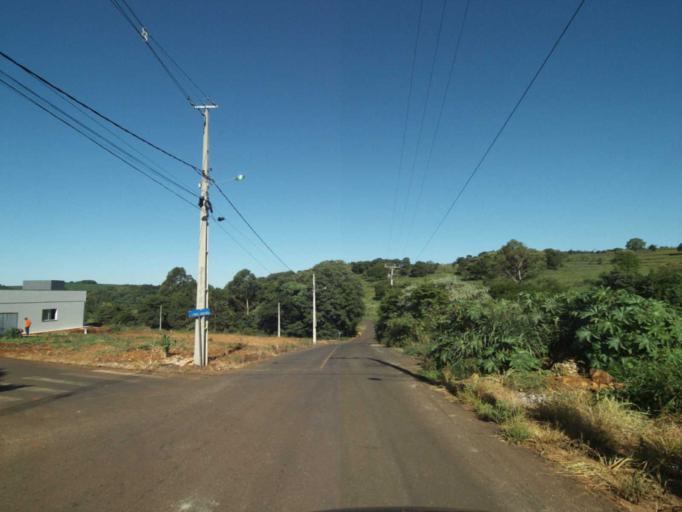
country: BR
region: Parana
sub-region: Coronel Vivida
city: Coronel Vivida
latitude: -25.9671
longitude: -52.8066
